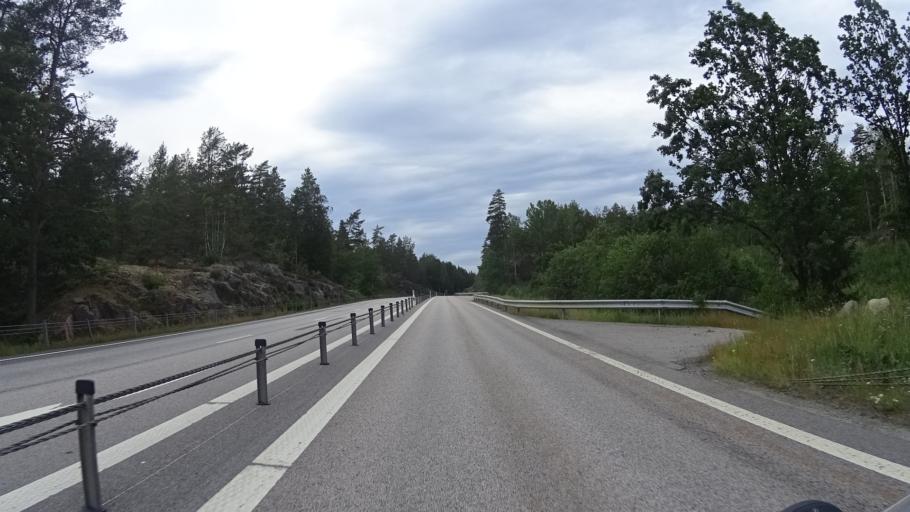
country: SE
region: Kalmar
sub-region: Vasterviks Kommun
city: Forserum
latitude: 58.0258
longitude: 16.5178
